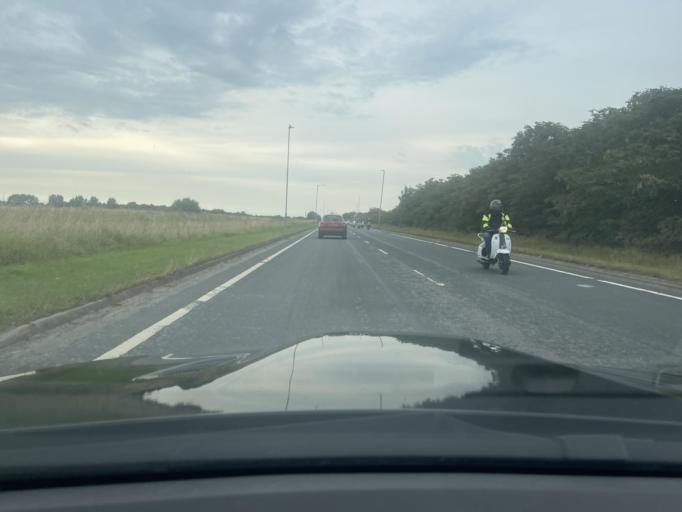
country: GB
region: England
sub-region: Lancashire
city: Leyland
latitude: 53.7078
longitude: -2.7166
